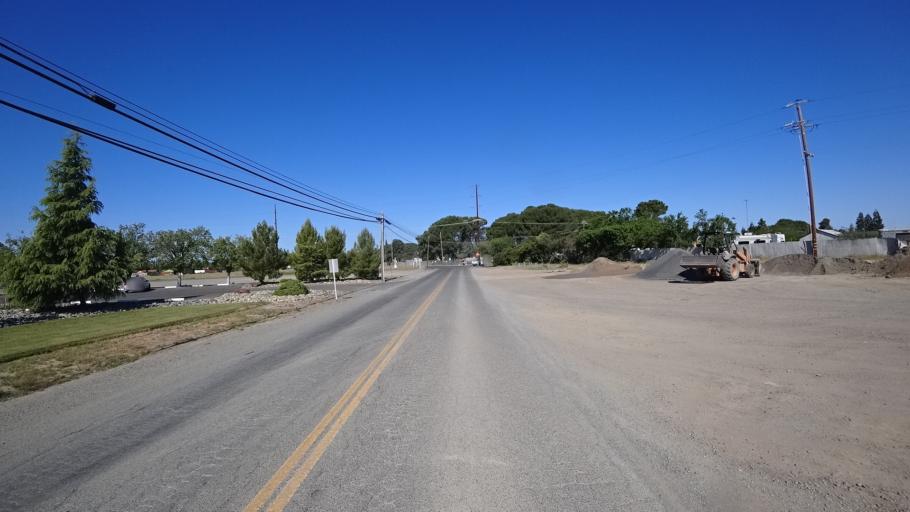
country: US
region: California
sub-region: Glenn County
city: Orland
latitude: 39.7396
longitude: -122.1771
